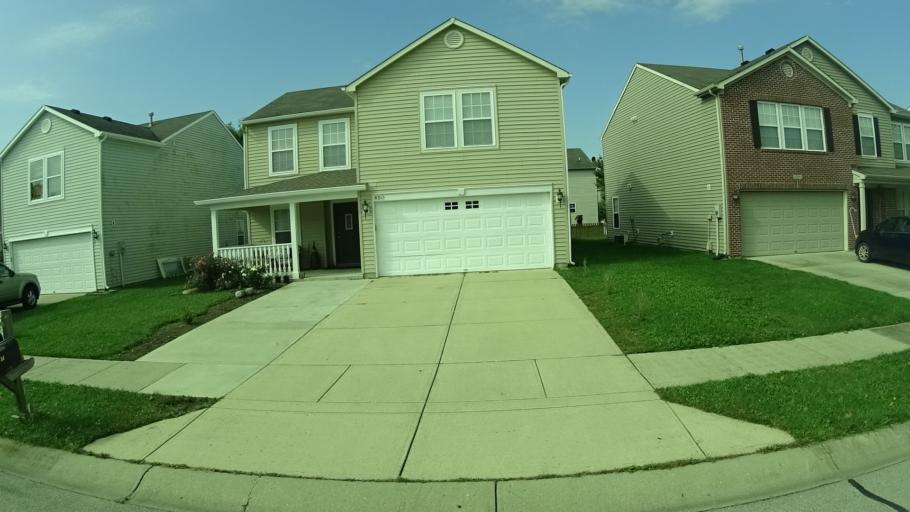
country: US
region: Indiana
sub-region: Hancock County
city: Fortville
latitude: 39.9833
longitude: -85.8498
